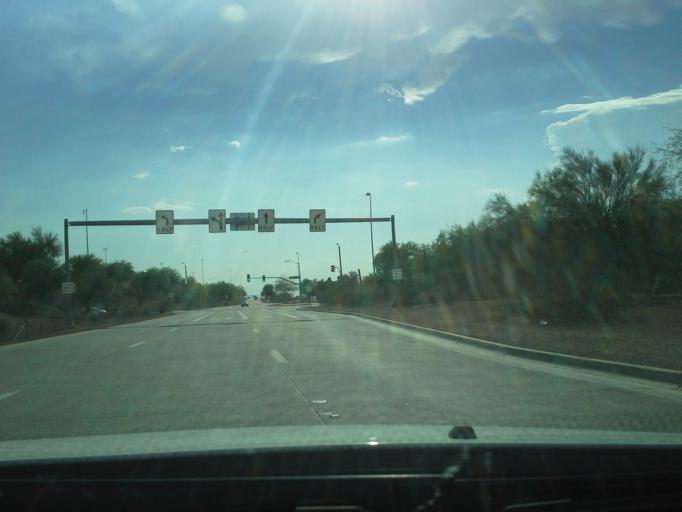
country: US
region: Arizona
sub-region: Maricopa County
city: Peoria
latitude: 33.6691
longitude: -112.1678
